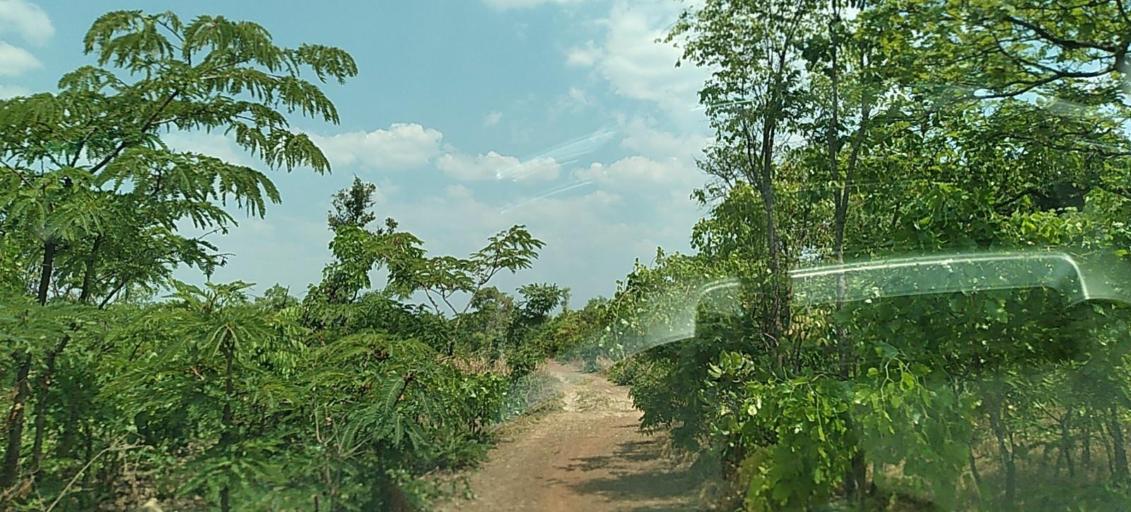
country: CD
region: Katanga
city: Kipushi
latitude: -12.0097
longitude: 27.4306
